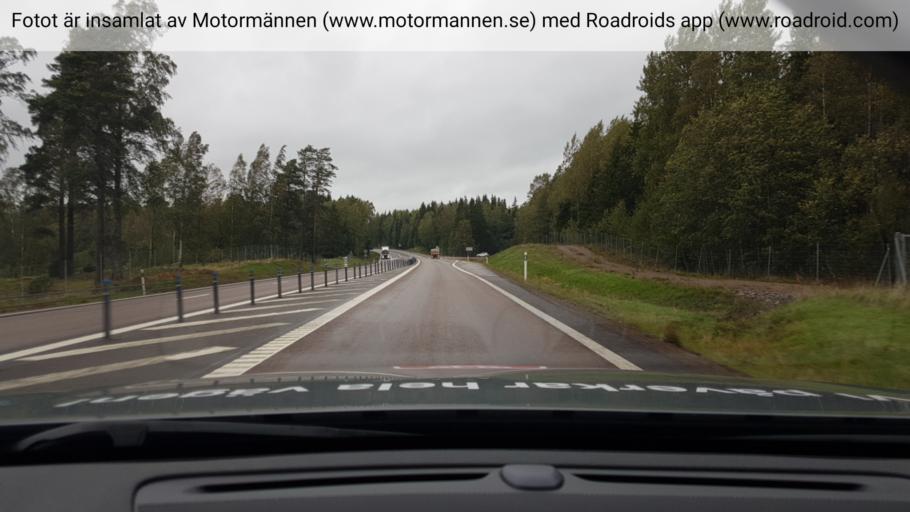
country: SE
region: Vaermland
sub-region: Kristinehamns Kommun
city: Kristinehamn
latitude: 59.3484
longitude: 14.0816
